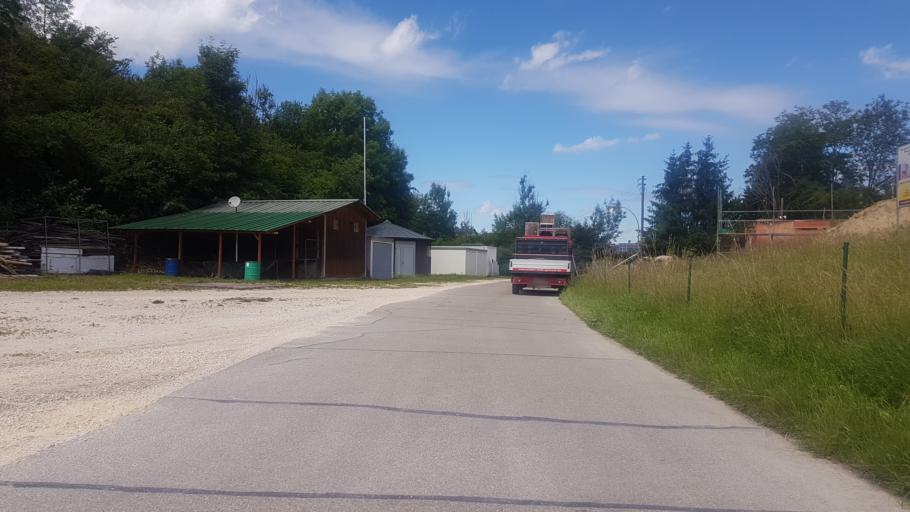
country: DE
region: Bavaria
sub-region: Swabia
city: Hochstadt an der Donau
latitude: 48.5927
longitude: 10.5420
